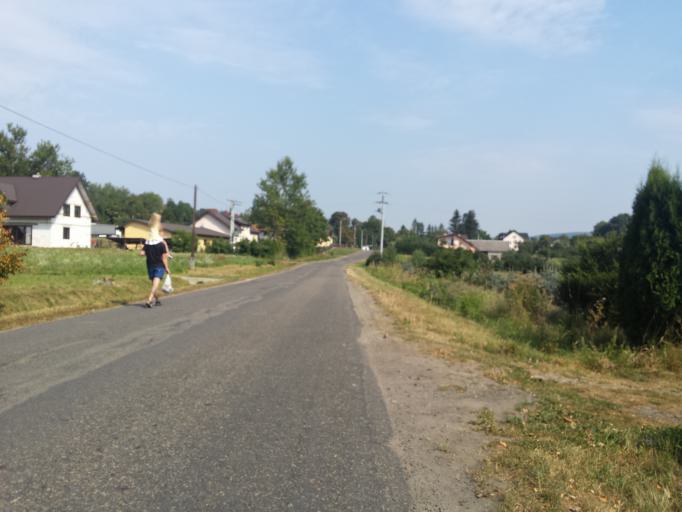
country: PL
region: Subcarpathian Voivodeship
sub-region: Powiat sanocki
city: Sanok
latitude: 49.6300
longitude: 22.2770
